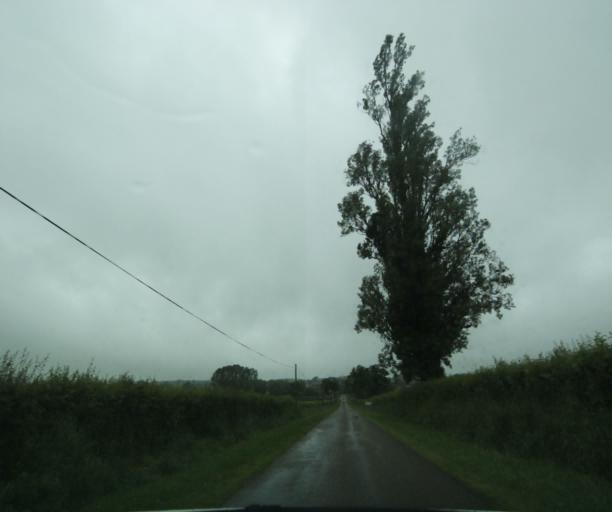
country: FR
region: Bourgogne
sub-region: Departement de Saone-et-Loire
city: Paray-le-Monial
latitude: 46.4775
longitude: 4.1777
